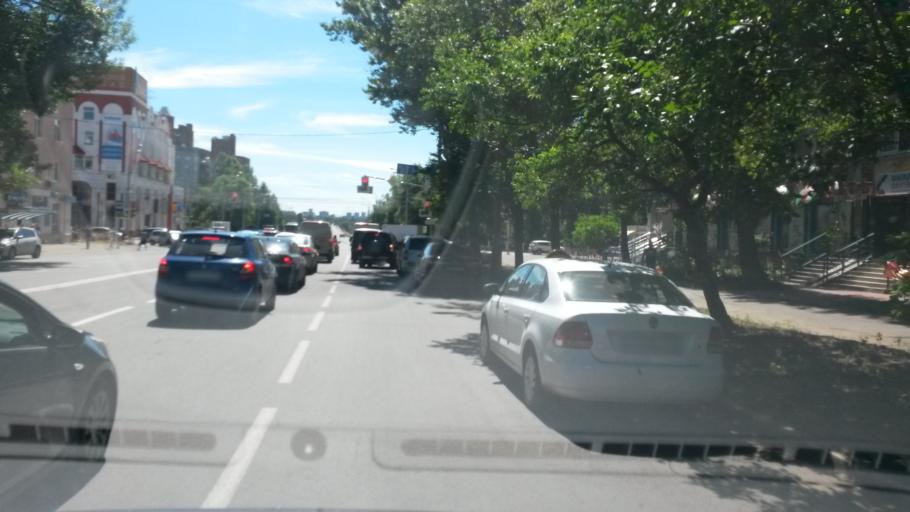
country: RU
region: Jaroslavl
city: Yaroslavl
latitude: 57.6217
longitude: 39.8580
